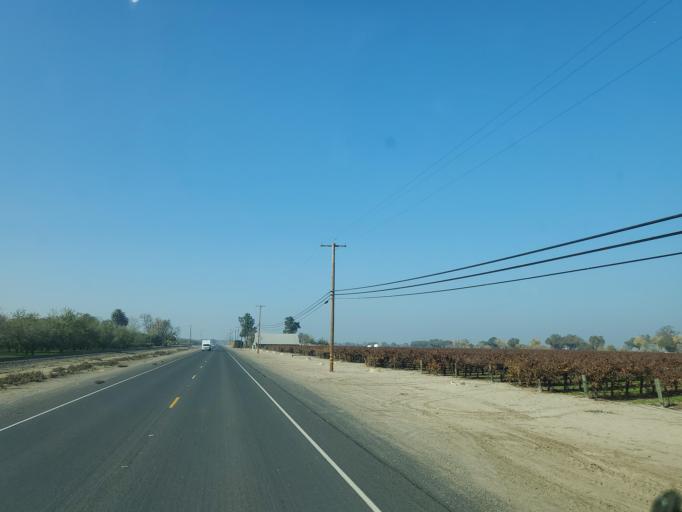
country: US
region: California
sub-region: San Joaquin County
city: Manteca
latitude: 37.8527
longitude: -121.1981
